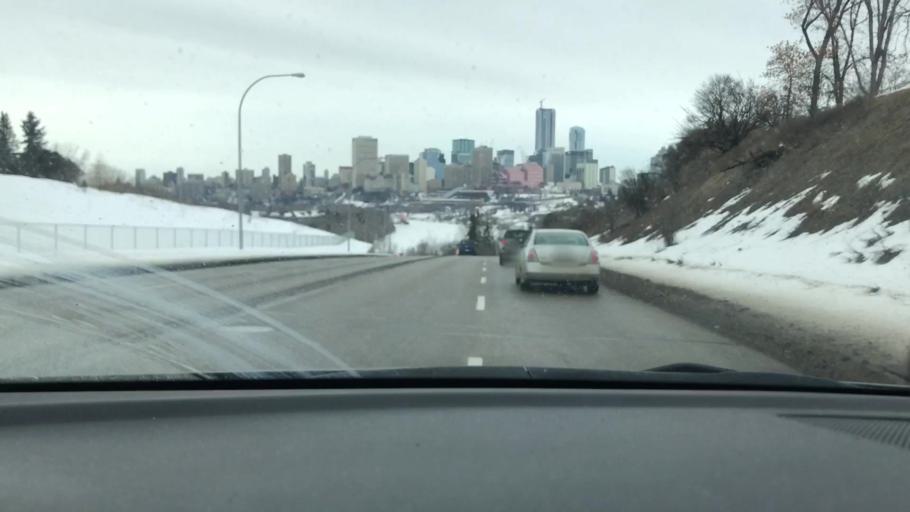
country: CA
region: Alberta
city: Edmonton
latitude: 53.5384
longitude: -113.4585
